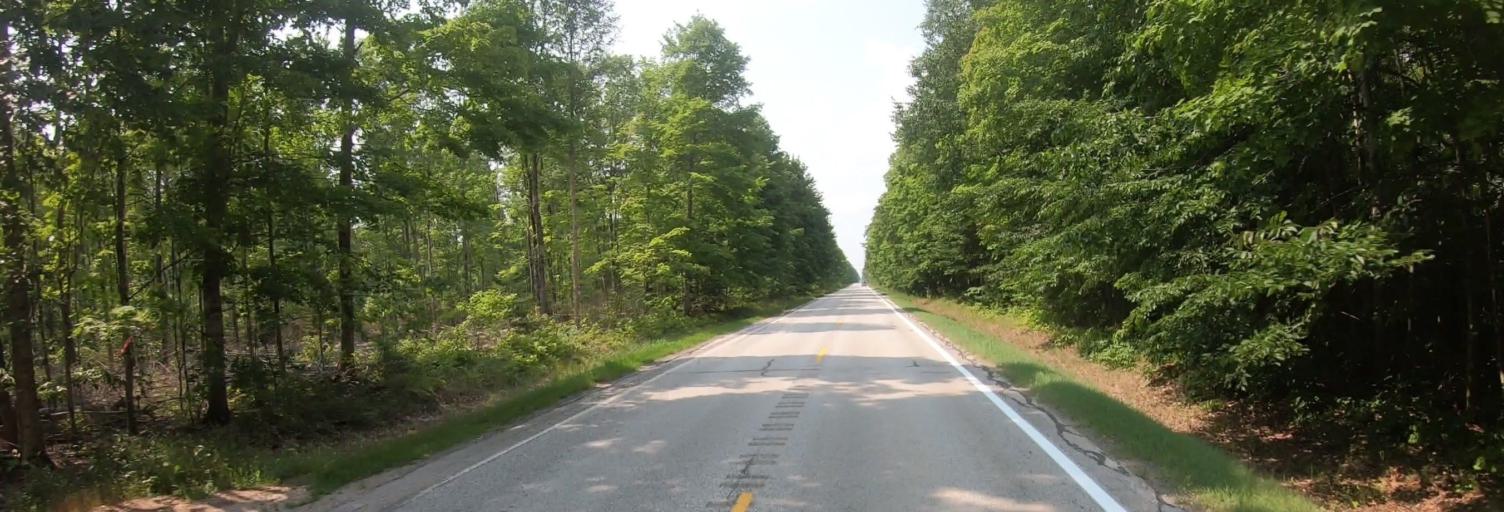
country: US
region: Michigan
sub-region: Luce County
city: Newberry
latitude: 46.5523
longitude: -85.3694
